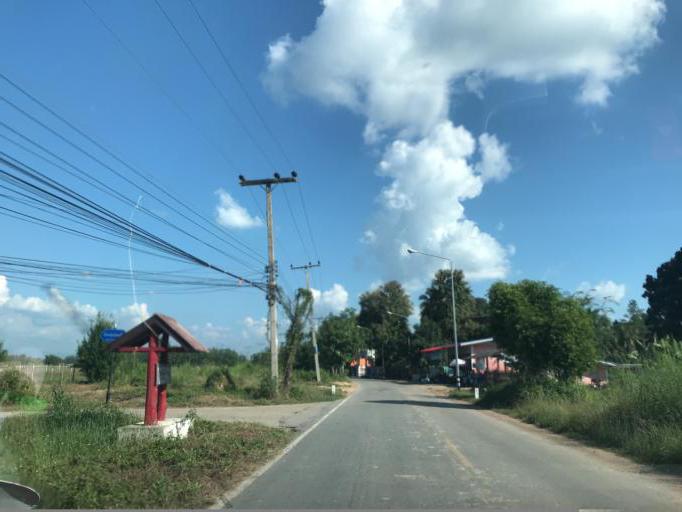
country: TH
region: Lamphun
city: Pa Sang
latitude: 18.5296
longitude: 98.8463
